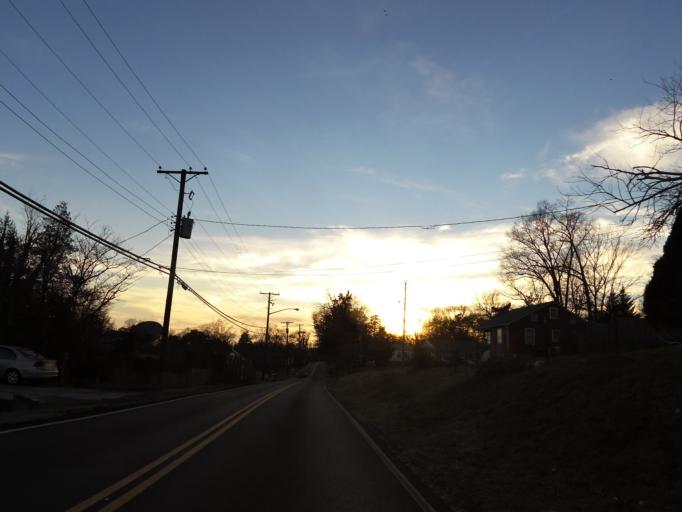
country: US
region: Tennessee
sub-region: Knox County
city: Knoxville
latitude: 36.0070
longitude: -83.9020
